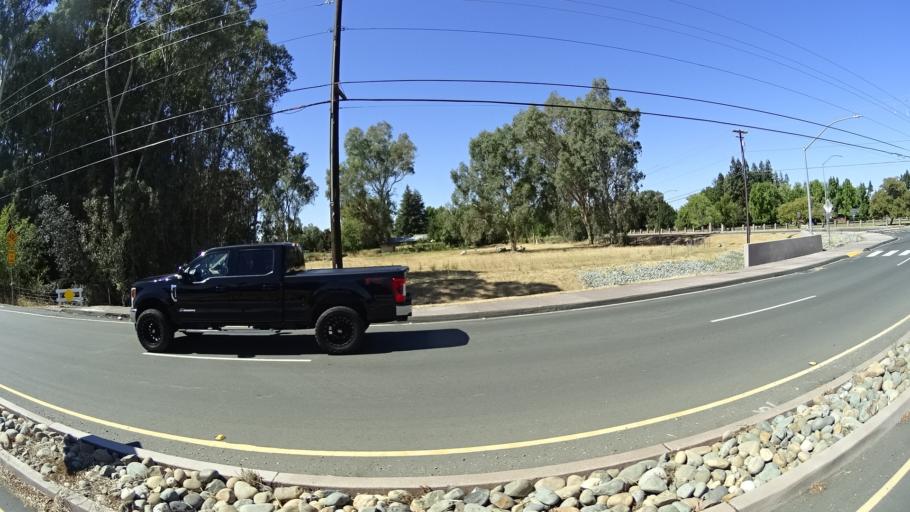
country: US
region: California
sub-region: Sacramento County
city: Vineyard
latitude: 38.4377
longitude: -121.3345
